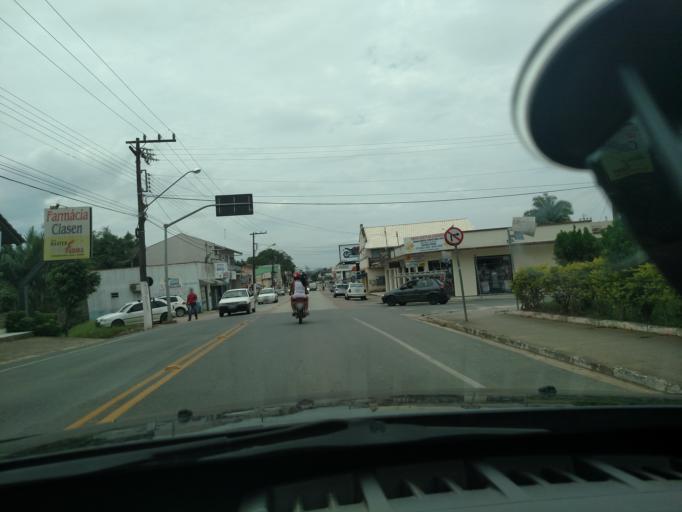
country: BR
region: Santa Catarina
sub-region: Gaspar
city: Gaspar
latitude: -26.9005
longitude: -48.8280
